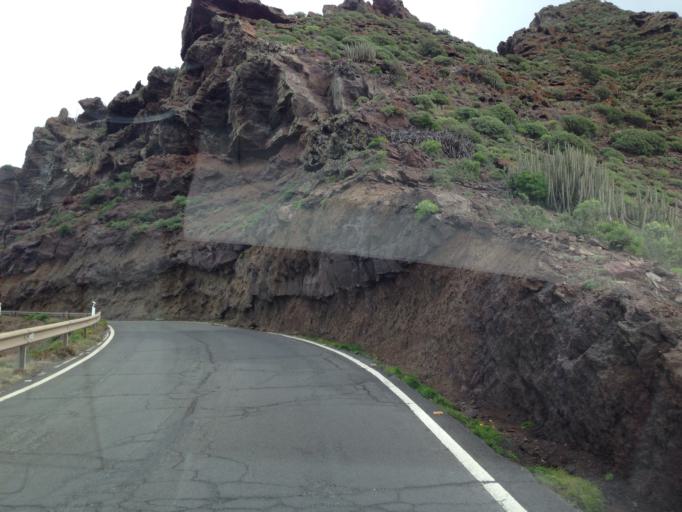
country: ES
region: Canary Islands
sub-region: Provincia de Las Palmas
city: San Nicolas
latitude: 28.0282
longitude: -15.7688
